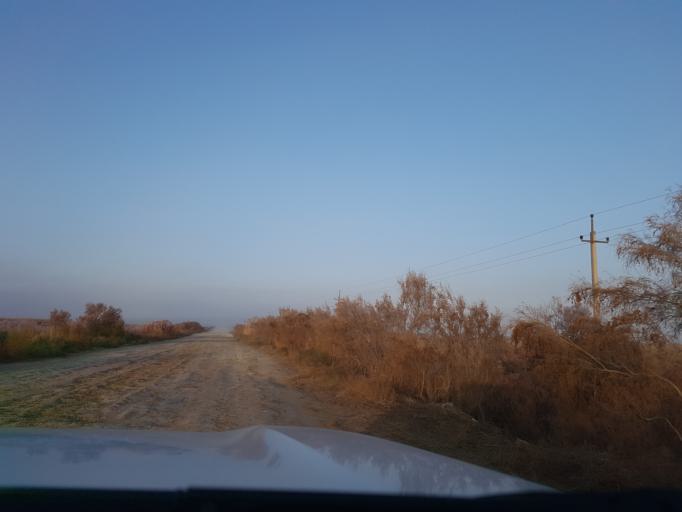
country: TM
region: Dasoguz
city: Koeneuergench
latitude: 41.8448
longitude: 58.5070
